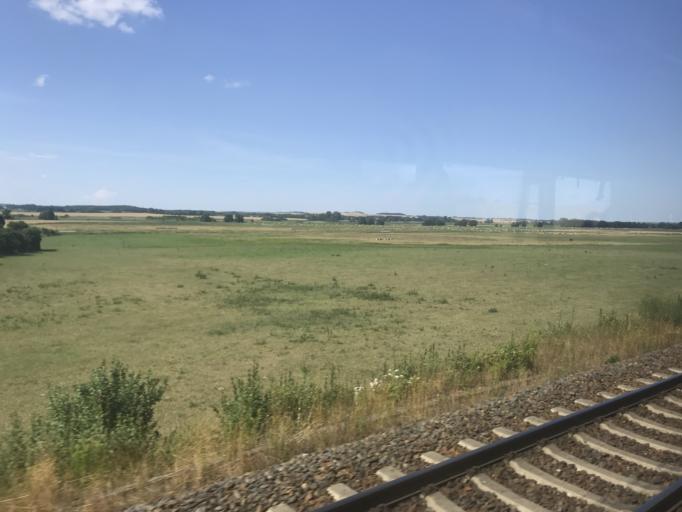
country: DE
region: Brandenburg
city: Angermunde
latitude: 53.0909
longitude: 14.0090
